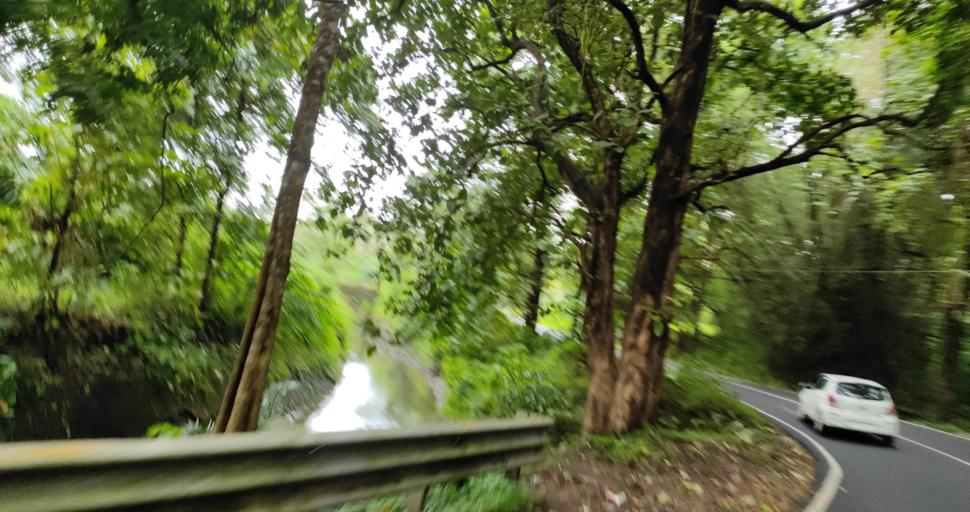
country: IN
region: Kerala
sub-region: Thrissur District
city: Kizhake Chalakudi
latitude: 10.3018
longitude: 76.4470
